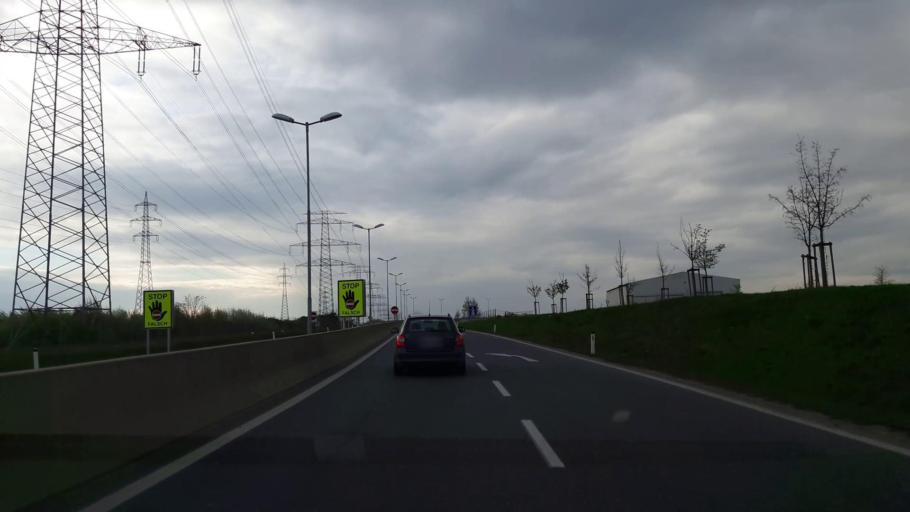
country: AT
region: Lower Austria
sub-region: Politischer Bezirk Mistelbach
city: Grossebersdorf
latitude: 48.3462
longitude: 16.4716
